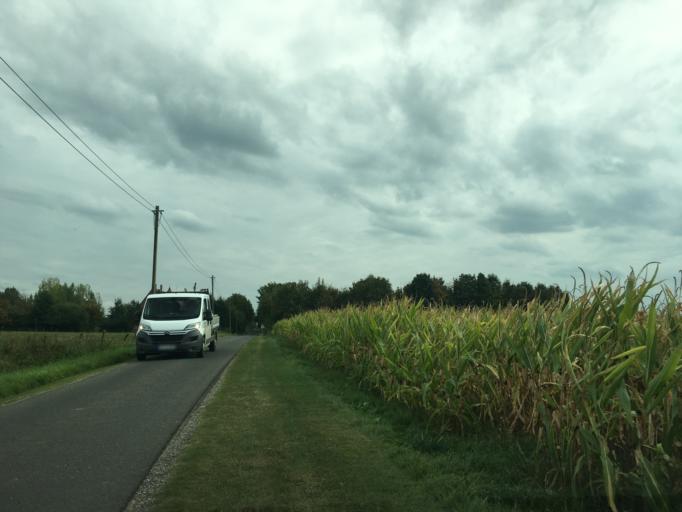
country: DE
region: North Rhine-Westphalia
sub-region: Regierungsbezirk Munster
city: Muenster
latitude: 51.9810
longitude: 7.5373
